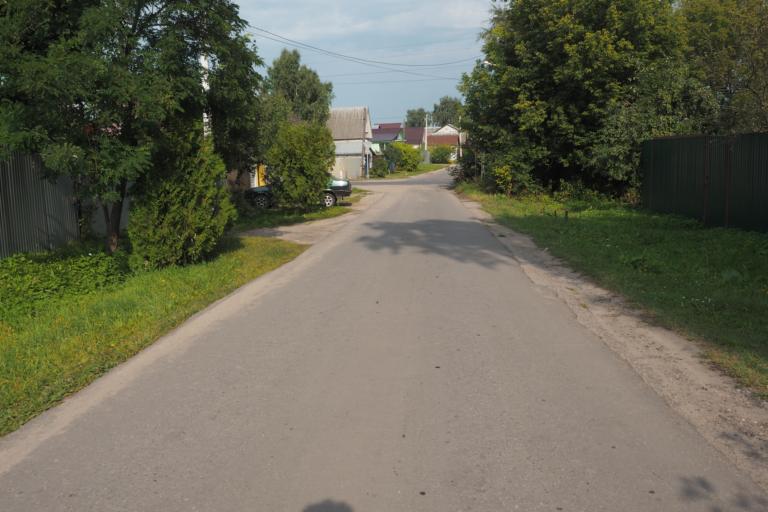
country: RU
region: Moskovskaya
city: Malyshevo
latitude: 55.5379
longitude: 38.3119
